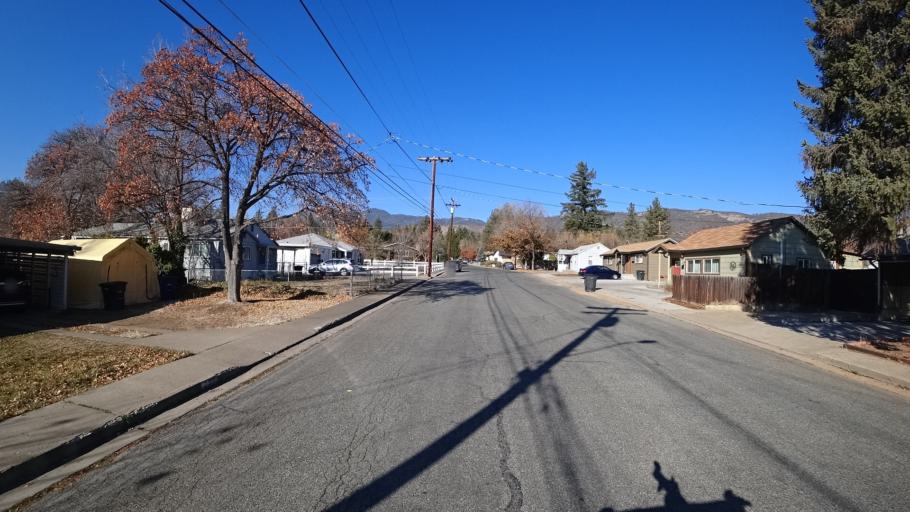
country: US
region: California
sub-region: Siskiyou County
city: Yreka
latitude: 41.7386
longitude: -122.6433
